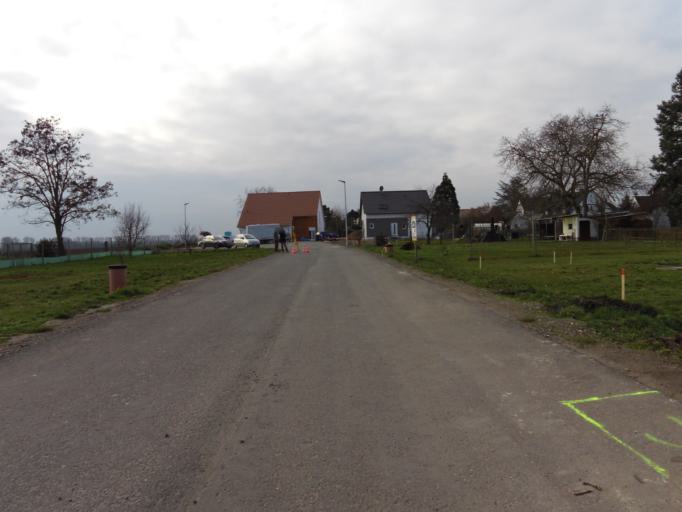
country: DE
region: Rheinland-Pfalz
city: Bobenheim-Roxheim
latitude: 49.6053
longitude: 8.3398
